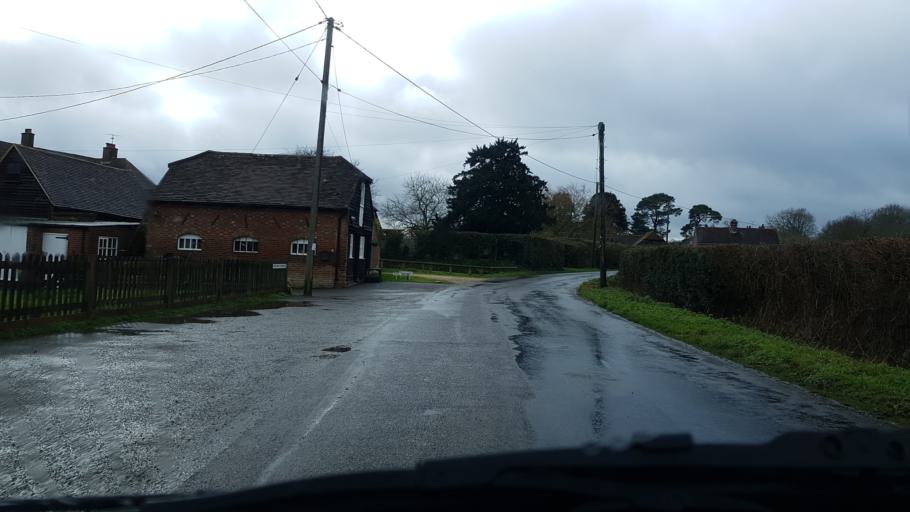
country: GB
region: England
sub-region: Surrey
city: Haslemere
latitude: 51.1078
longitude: -0.6687
